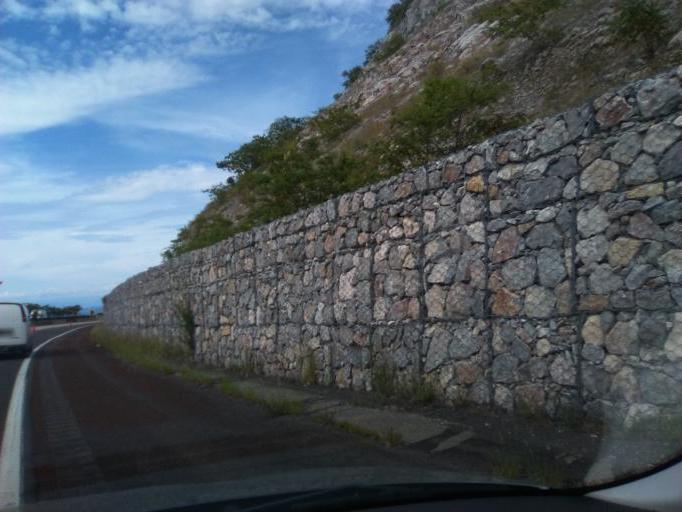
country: MX
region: Guerrero
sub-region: Eduardo Neri
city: Tlanipatla
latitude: 17.8522
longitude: -99.4062
